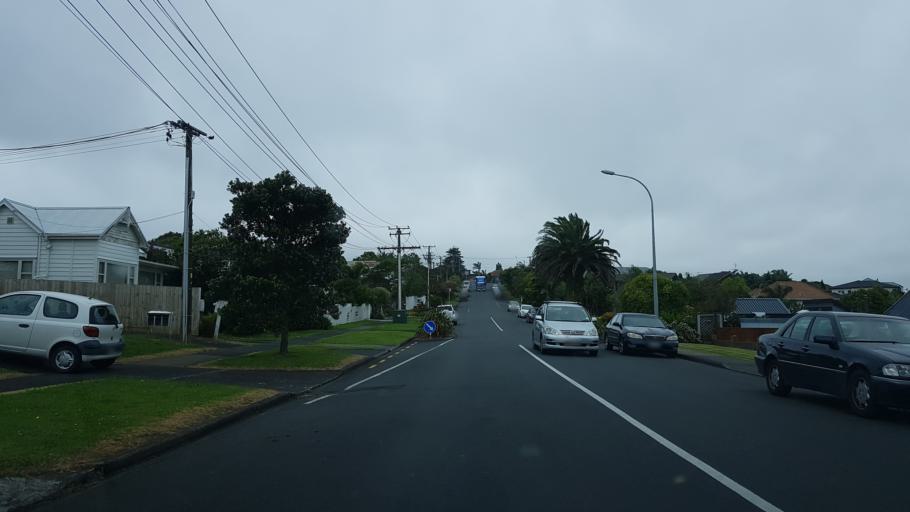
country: NZ
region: Auckland
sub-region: Auckland
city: North Shore
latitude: -36.8130
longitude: 174.7093
